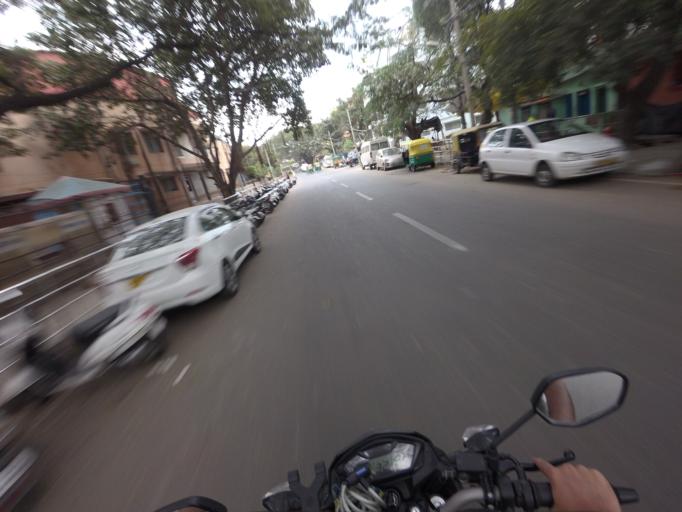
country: IN
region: Karnataka
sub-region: Bangalore Urban
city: Bangalore
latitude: 12.9613
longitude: 77.5405
